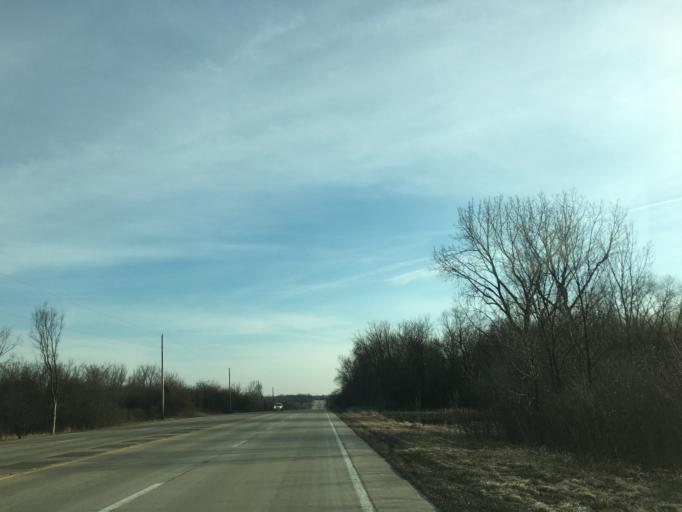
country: US
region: Illinois
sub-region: Cook County
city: Streamwood
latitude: 42.0514
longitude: -88.1790
